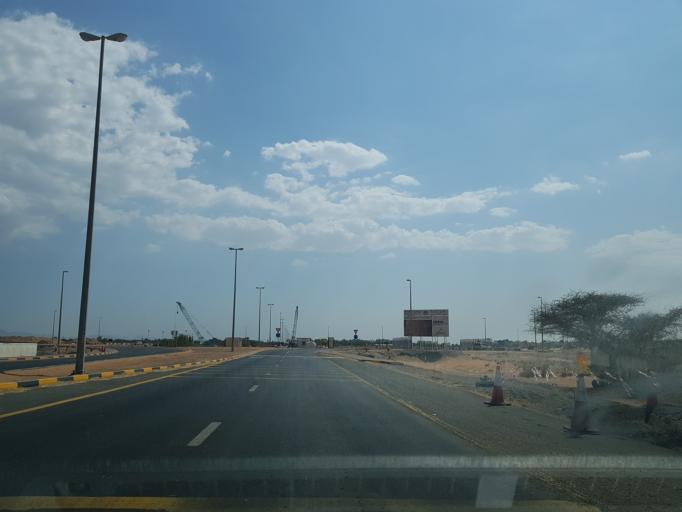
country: AE
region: Ash Shariqah
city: Adh Dhayd
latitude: 25.2340
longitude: 55.9168
